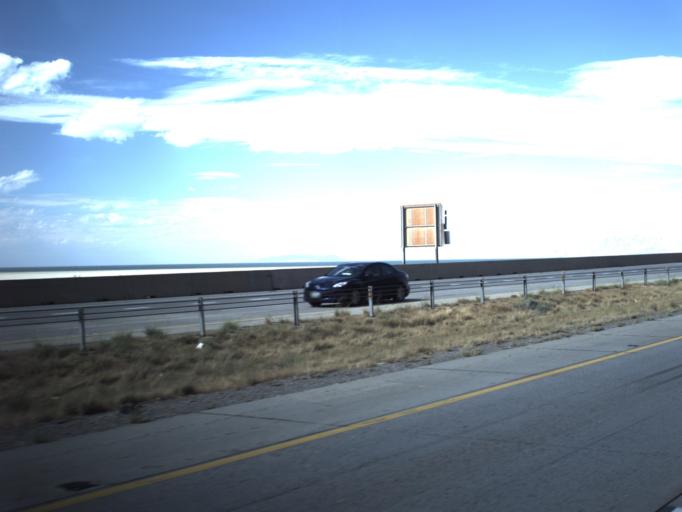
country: US
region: Utah
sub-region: Tooele County
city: Stansbury park
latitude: 40.7038
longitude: -112.2561
